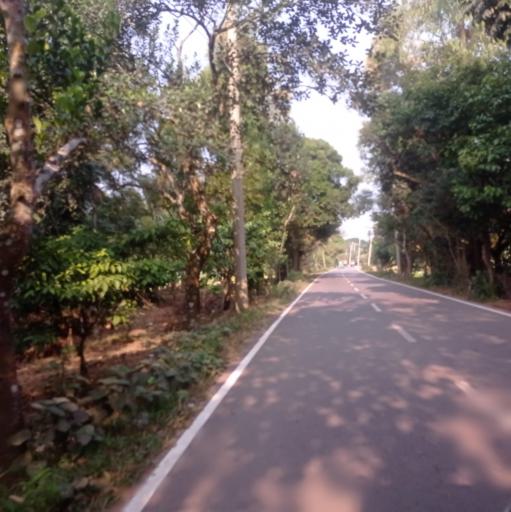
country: BD
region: Dhaka
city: Bhairab Bazar
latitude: 24.0721
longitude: 90.8434
